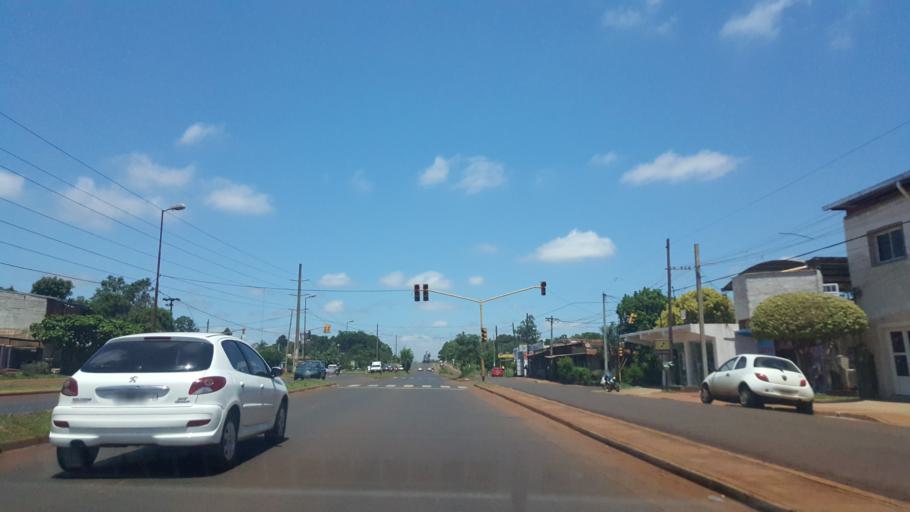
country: AR
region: Misiones
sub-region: Departamento de Capital
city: Posadas
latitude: -27.4067
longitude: -55.9240
